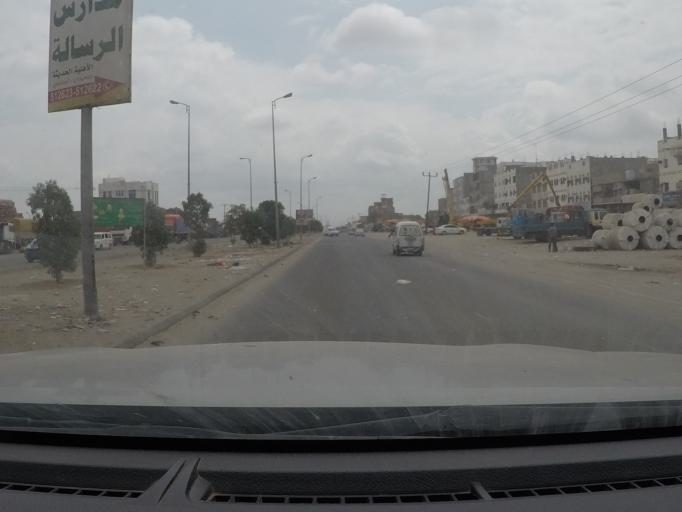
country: YE
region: Lahij
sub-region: Al  Hawtah
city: Lahij
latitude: 12.9905
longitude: 44.9334
